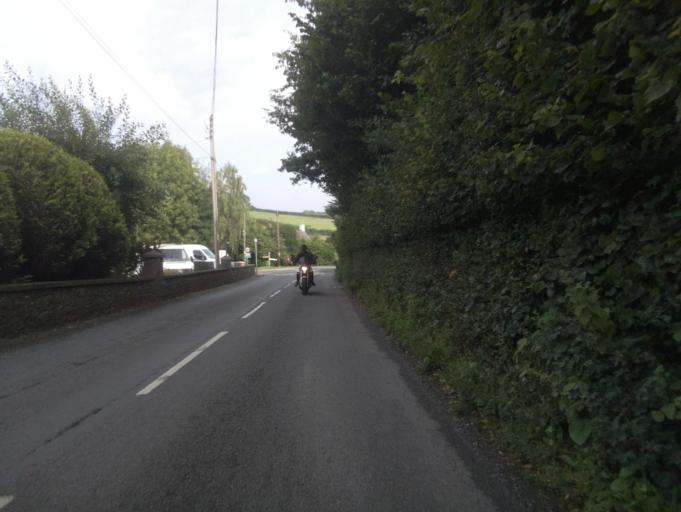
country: GB
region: England
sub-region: Bath and North East Somerset
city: East Harptree
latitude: 51.2808
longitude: -2.5872
